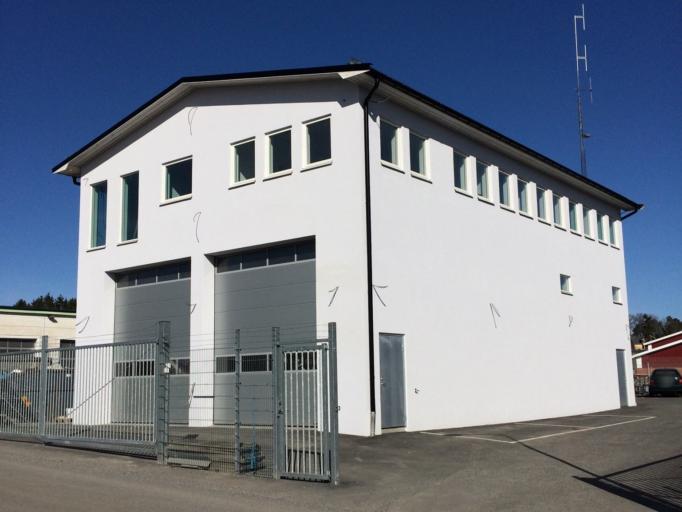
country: SE
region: Stockholm
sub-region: Ekero Kommun
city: Ekeroe
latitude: 59.2841
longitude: 17.8292
